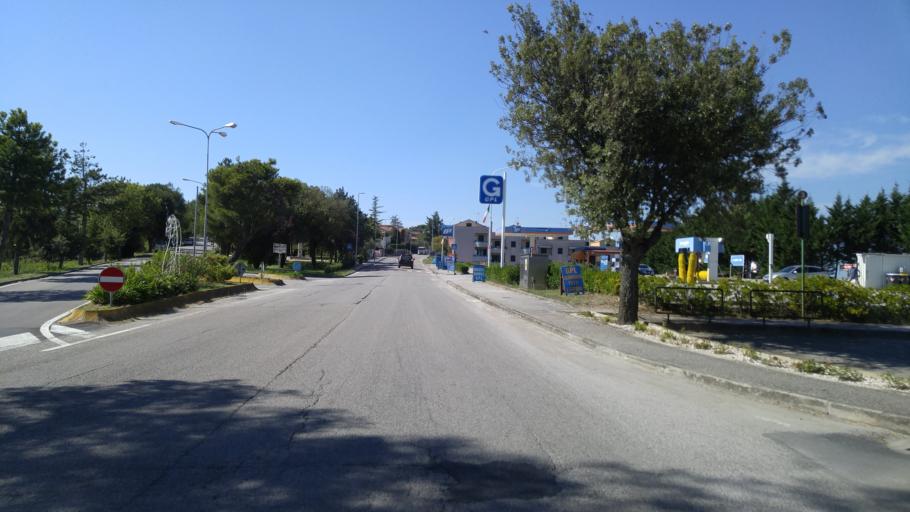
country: IT
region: The Marches
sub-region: Provincia di Pesaro e Urbino
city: San Giorgio di Pesaro
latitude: 43.7150
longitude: 12.9845
